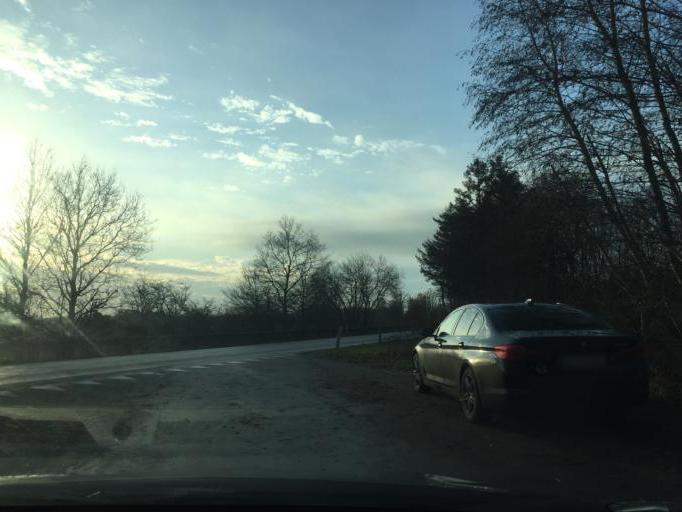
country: DK
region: South Denmark
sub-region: Faaborg-Midtfyn Kommune
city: Faaborg
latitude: 55.1673
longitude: 10.2782
